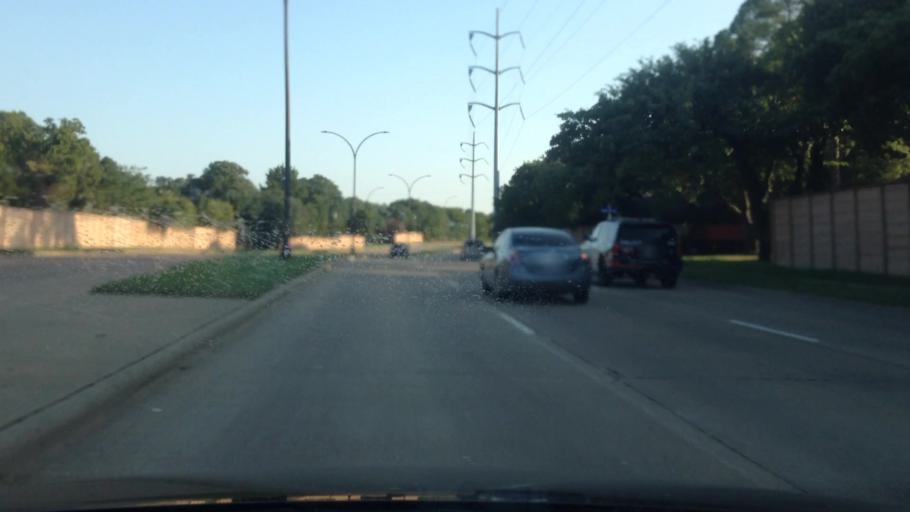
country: US
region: Texas
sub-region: Tarrant County
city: Dalworthington Gardens
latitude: 32.6932
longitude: -97.1904
